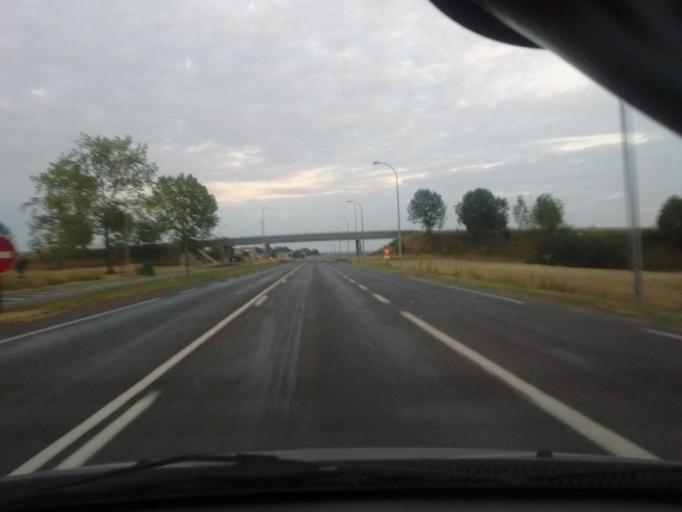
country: FR
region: Ile-de-France
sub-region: Departement de Seine-et-Marne
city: Pringy
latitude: 48.5035
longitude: 2.5764
